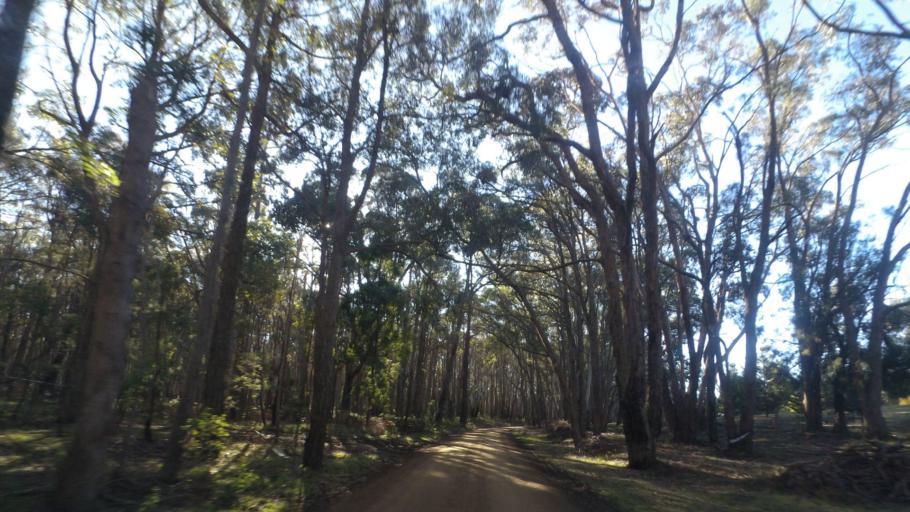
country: AU
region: Victoria
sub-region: Mount Alexander
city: Castlemaine
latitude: -37.2884
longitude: 144.3306
